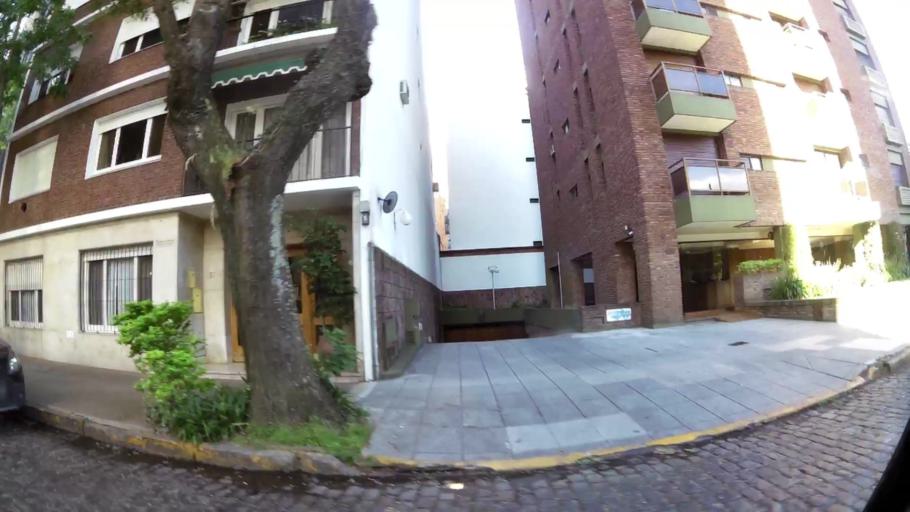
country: AR
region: Buenos Aires
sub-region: Partido de San Isidro
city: San Isidro
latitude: -34.4730
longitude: -58.5106
